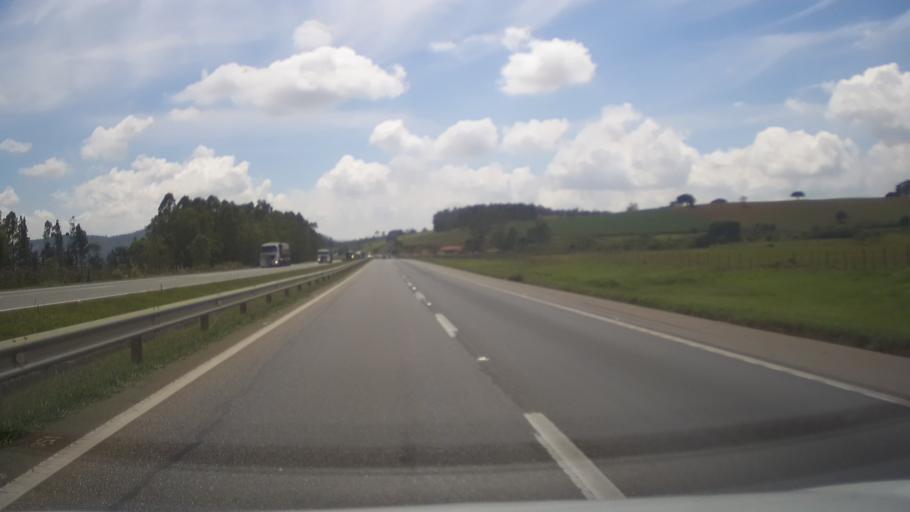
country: BR
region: Minas Gerais
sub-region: Santa Rita Do Sapucai
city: Santa Rita do Sapucai
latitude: -22.0975
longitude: -45.7172
